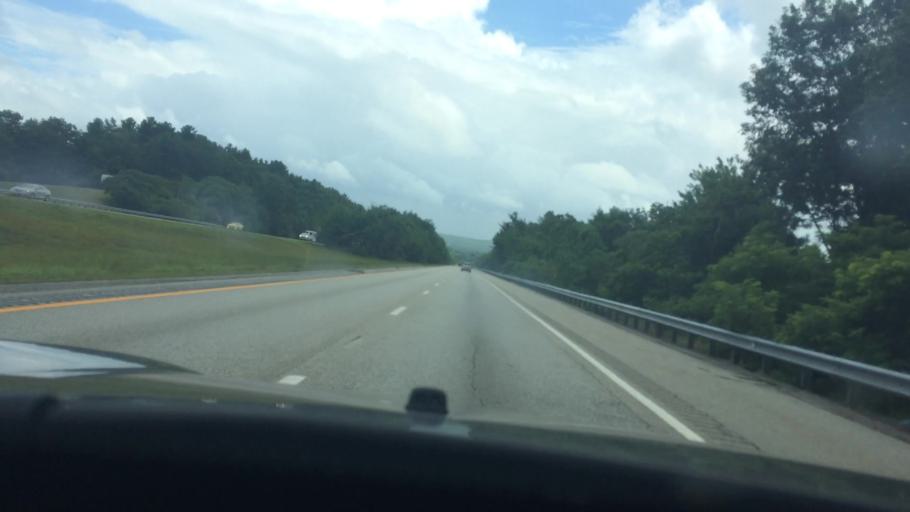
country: US
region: Massachusetts
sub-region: Worcester County
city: Westminster
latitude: 42.5546
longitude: -71.9200
